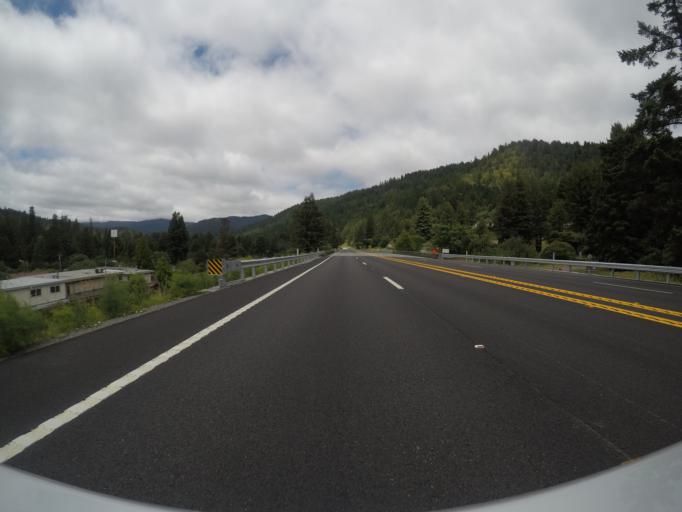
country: US
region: California
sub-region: Humboldt County
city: Redway
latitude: 40.3209
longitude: -123.9213
